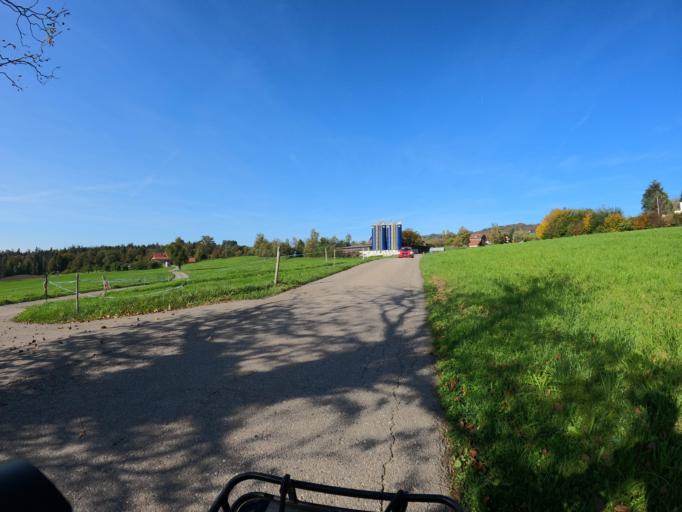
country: CH
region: Zug
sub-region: Zug
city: Baar
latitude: 47.2141
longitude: 8.5562
